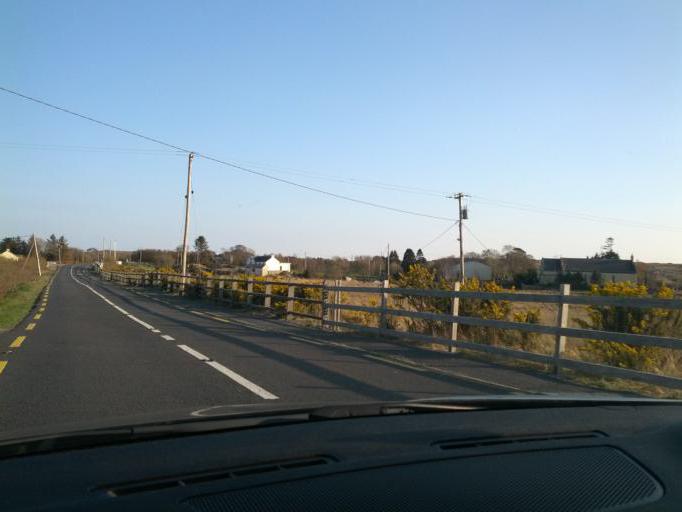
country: IE
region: Connaught
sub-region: County Galway
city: Oughterard
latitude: 53.3775
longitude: -9.5472
